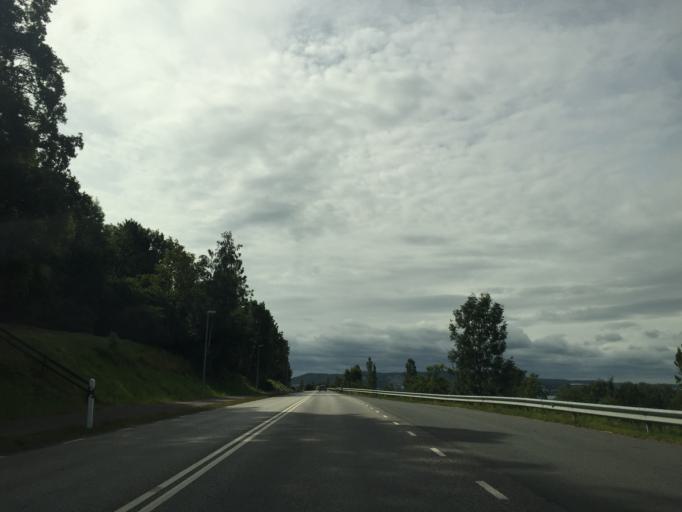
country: SE
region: Joenkoeping
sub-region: Jonkopings Kommun
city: Kaxholmen
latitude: 57.8263
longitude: 14.2706
